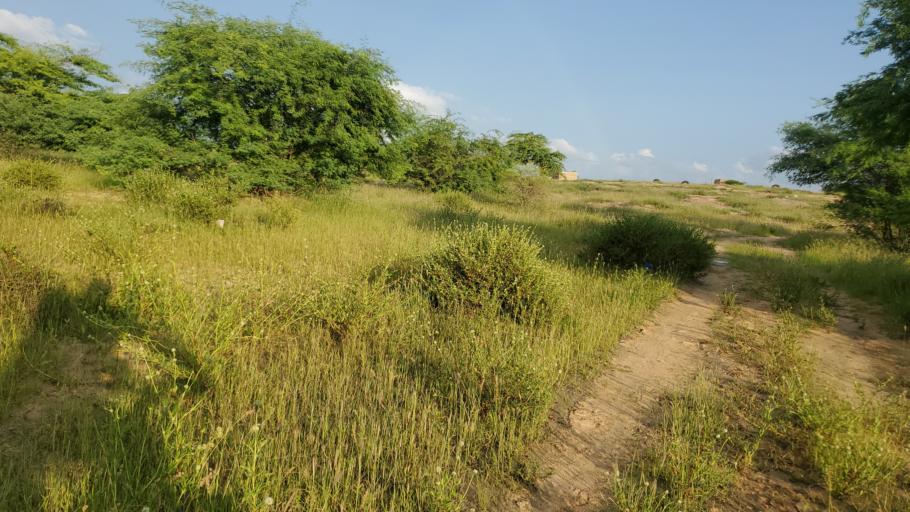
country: SN
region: Saint-Louis
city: Saint-Louis
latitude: 16.0496
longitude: -16.4193
